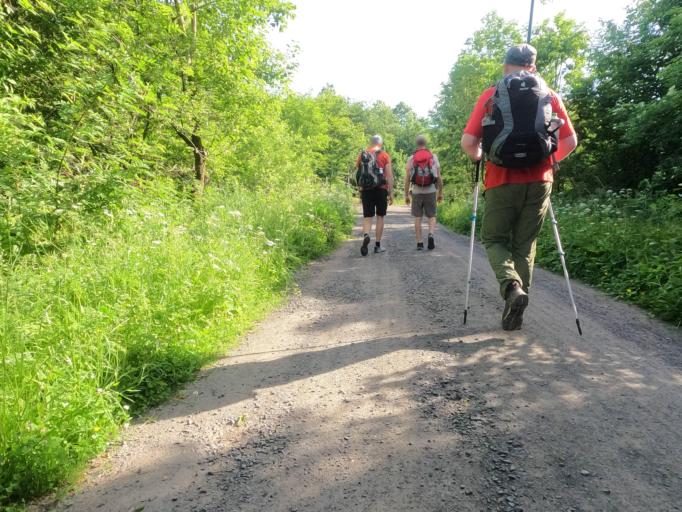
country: DE
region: Rheinland-Pfalz
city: Bad Marienberg
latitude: 50.6615
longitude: 7.9444
